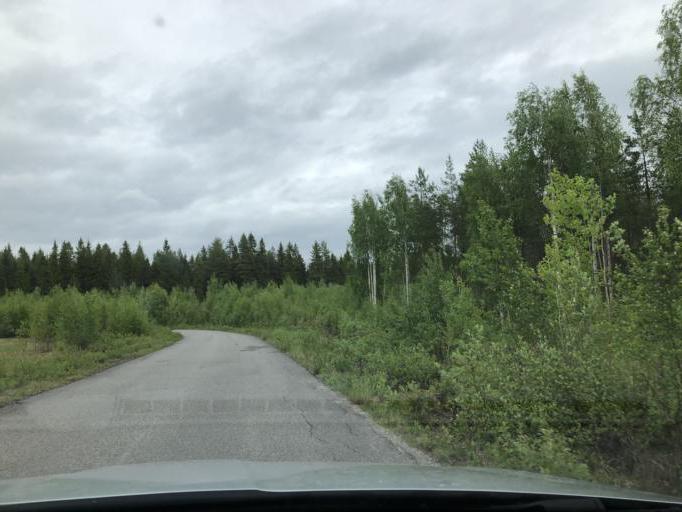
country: SE
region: Norrbotten
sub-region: Pitea Kommun
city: Roknas
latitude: 65.3865
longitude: 21.2689
